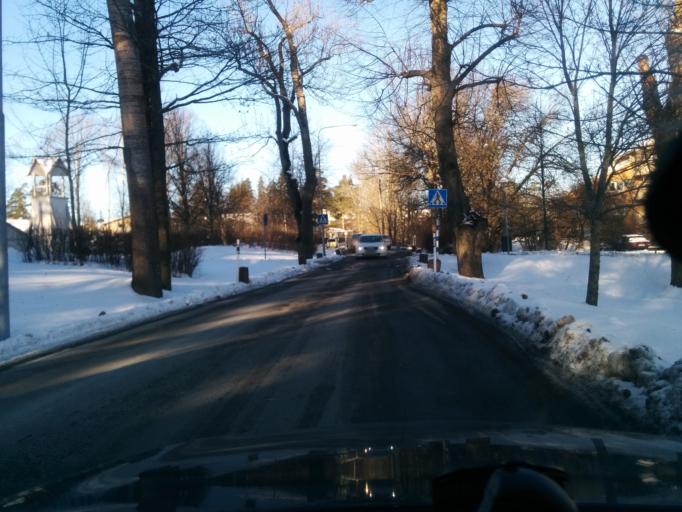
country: SE
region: Stockholm
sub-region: Taby Kommun
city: Taby
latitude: 59.4623
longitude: 18.0873
